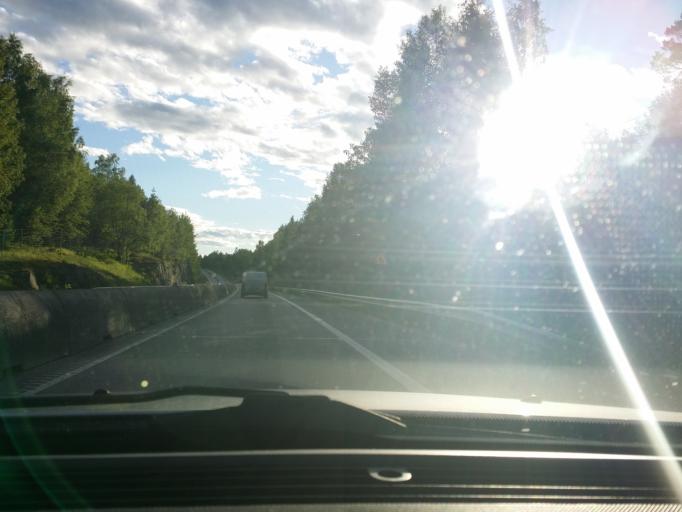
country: SE
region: Stockholm
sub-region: Jarfalla Kommun
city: Jakobsberg
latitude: 59.4778
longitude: 17.8419
